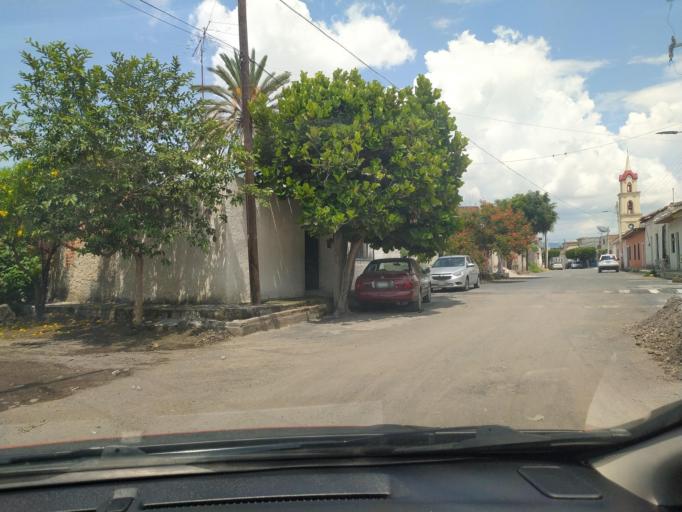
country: MX
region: Jalisco
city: Villa Corona
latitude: 20.3525
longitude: -103.6736
